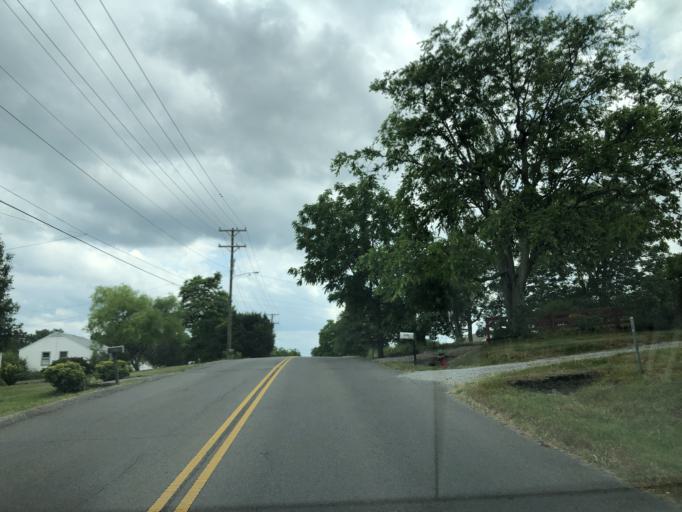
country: US
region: Tennessee
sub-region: Davidson County
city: Lakewood
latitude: 36.2608
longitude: -86.6910
